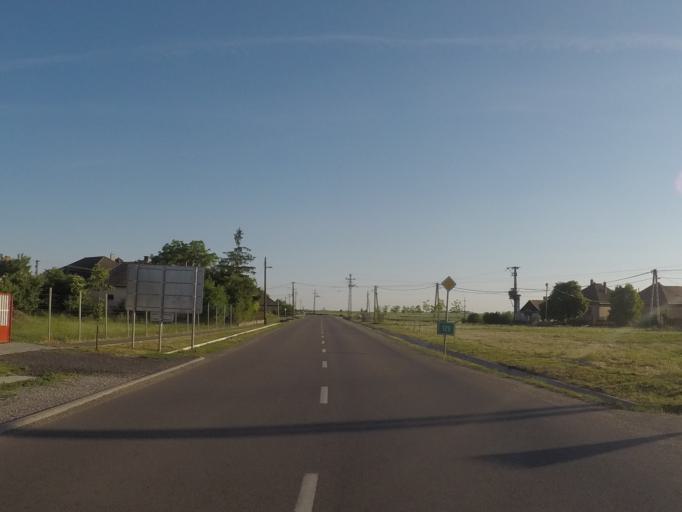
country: HU
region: Heves
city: Besenyotelek
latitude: 47.7203
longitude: 20.4154
